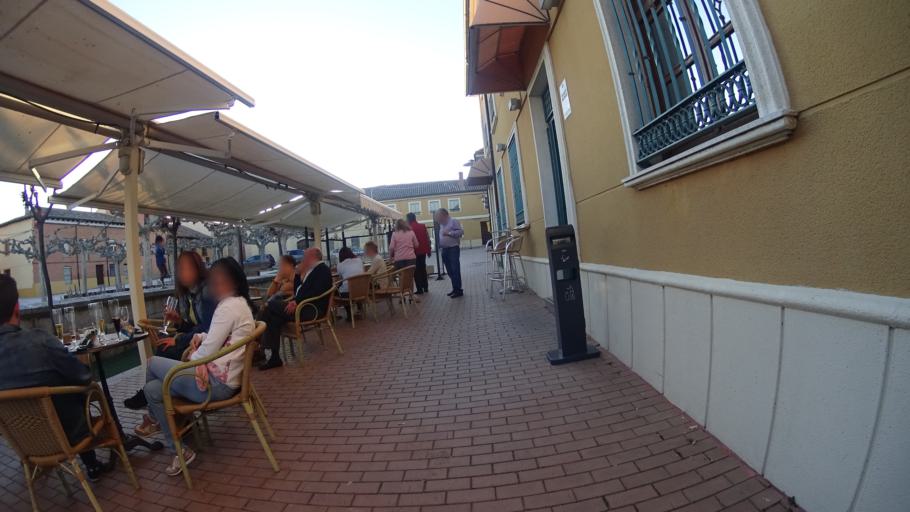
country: ES
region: Castille and Leon
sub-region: Provincia de Palencia
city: Fromista
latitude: 42.2671
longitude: -4.4070
